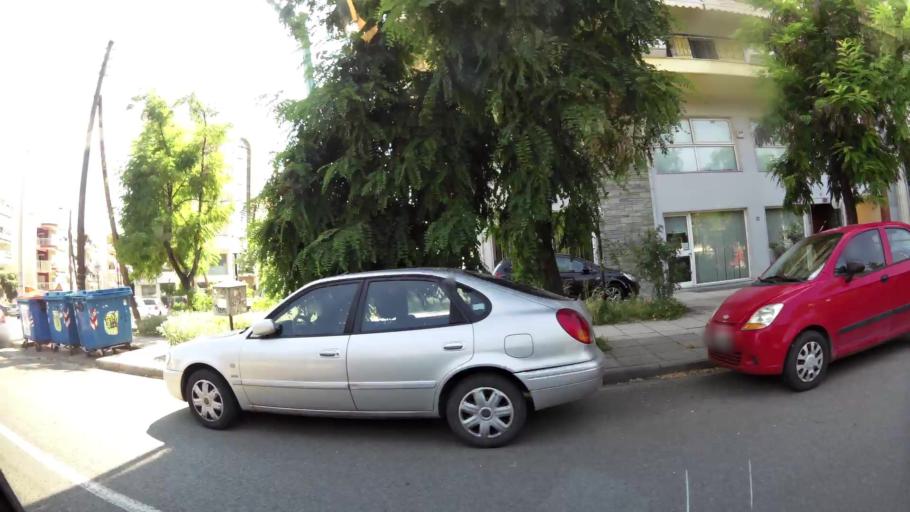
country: GR
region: Central Macedonia
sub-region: Nomos Thessalonikis
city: Kalamaria
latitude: 40.5917
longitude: 22.9541
